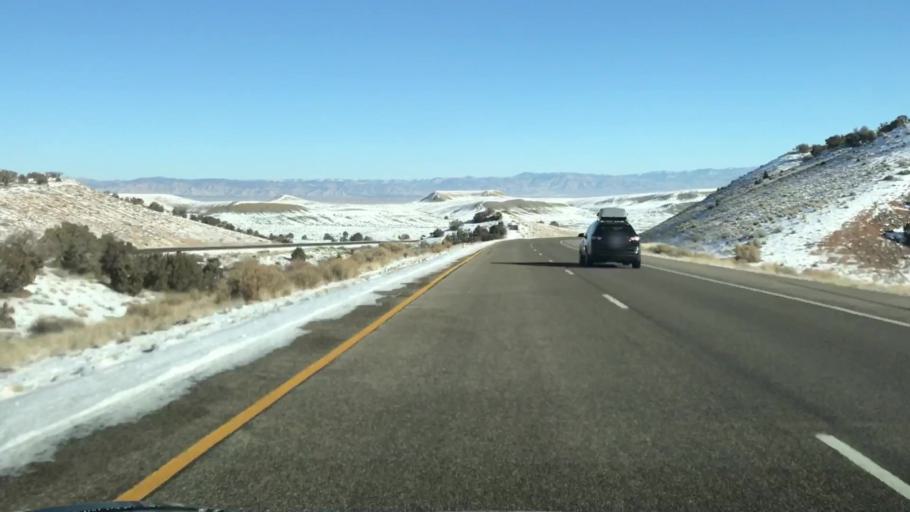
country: US
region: Colorado
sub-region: Mesa County
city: Loma
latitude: 39.2182
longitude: -108.9606
